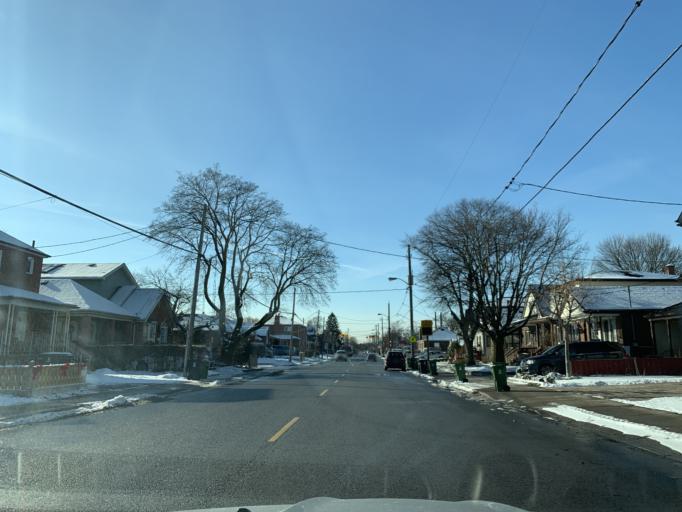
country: CA
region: Ontario
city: Toronto
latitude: 43.6834
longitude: -79.4876
